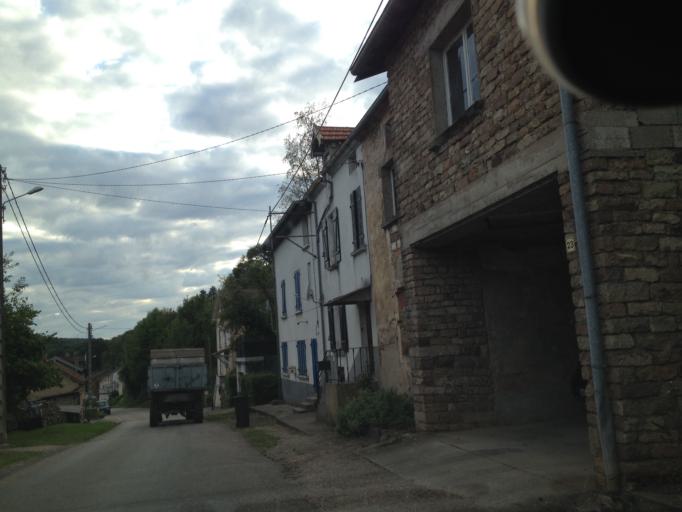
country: FR
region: Lorraine
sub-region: Departement des Vosges
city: Bains-les-Bains
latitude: 47.9781
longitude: 6.2037
